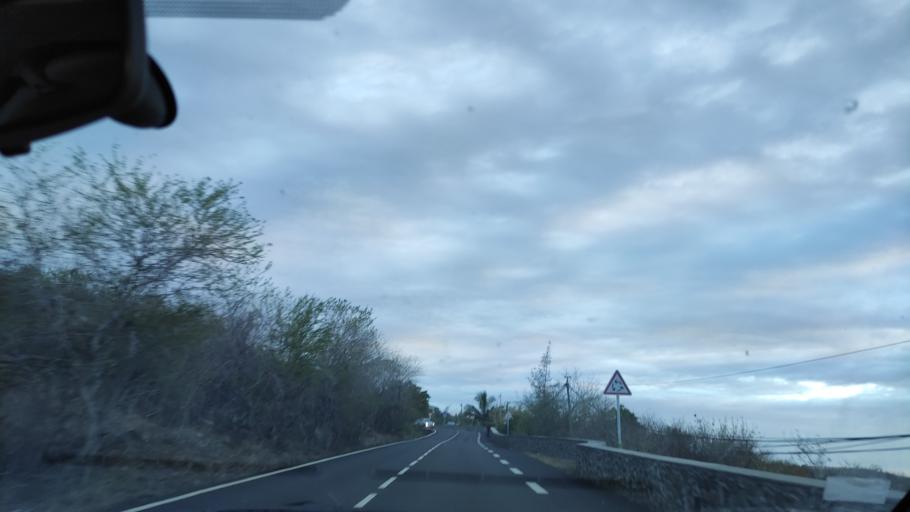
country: RE
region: Reunion
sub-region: Reunion
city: Saint-Leu
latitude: -21.1911
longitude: 55.2899
